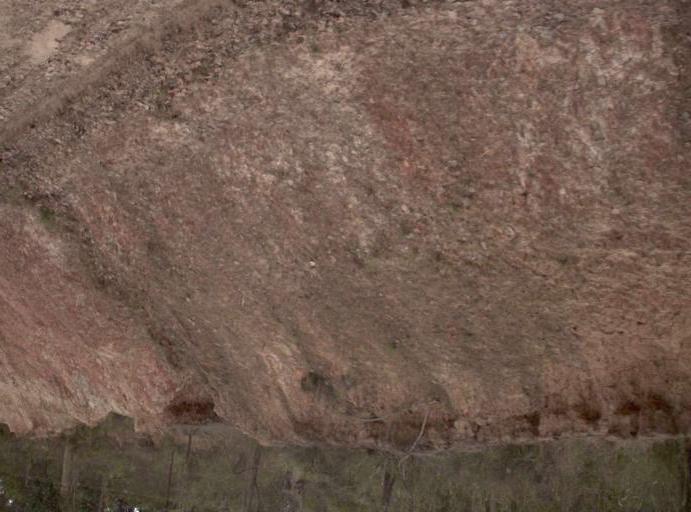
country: AU
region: Victoria
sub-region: Wellington
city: Sale
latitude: -38.0120
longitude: 147.1890
